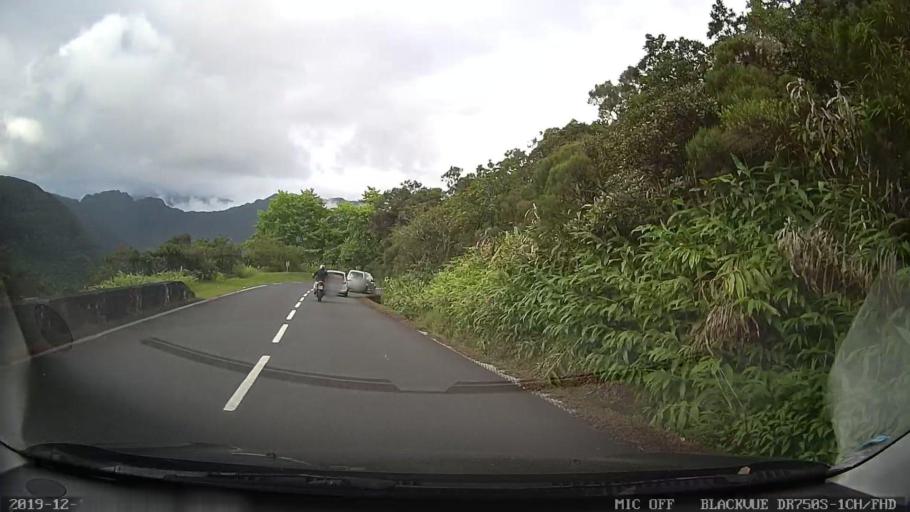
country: RE
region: Reunion
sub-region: Reunion
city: Cilaos
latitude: -21.1606
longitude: 55.5961
